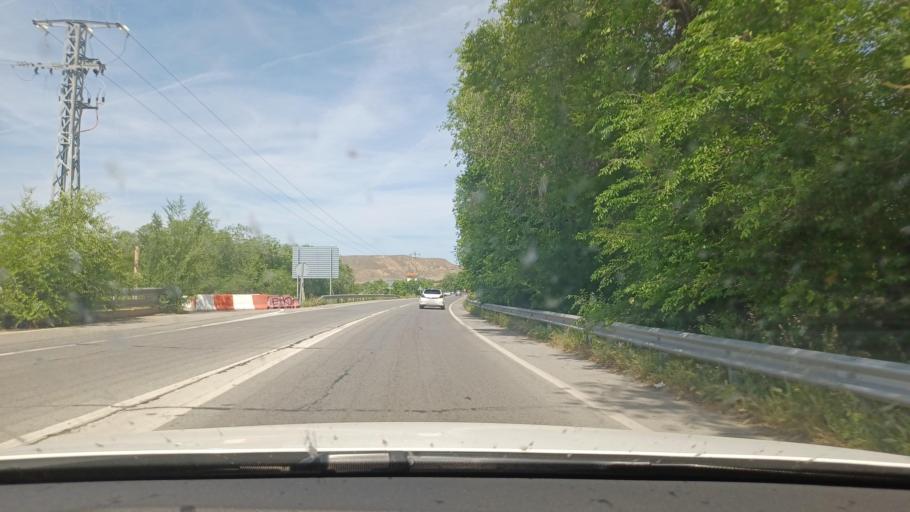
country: ES
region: Madrid
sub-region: Provincia de Madrid
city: Torrejon de Ardoz
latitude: 40.4308
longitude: -3.4443
